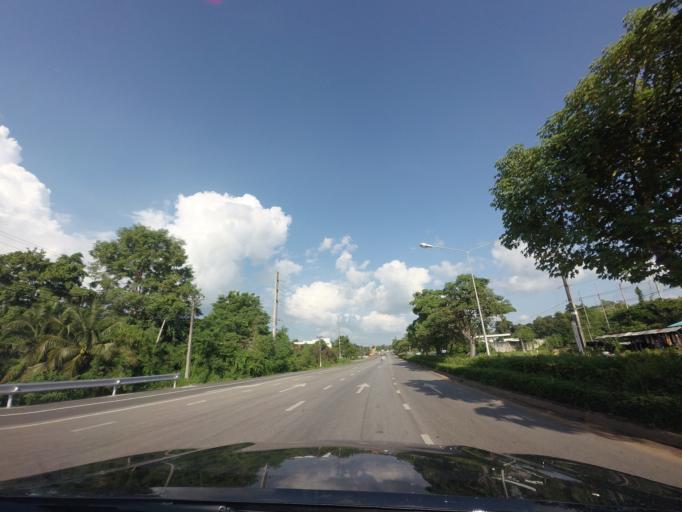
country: TH
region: Nong Khai
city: Nong Khai
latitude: 17.8876
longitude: 102.7645
